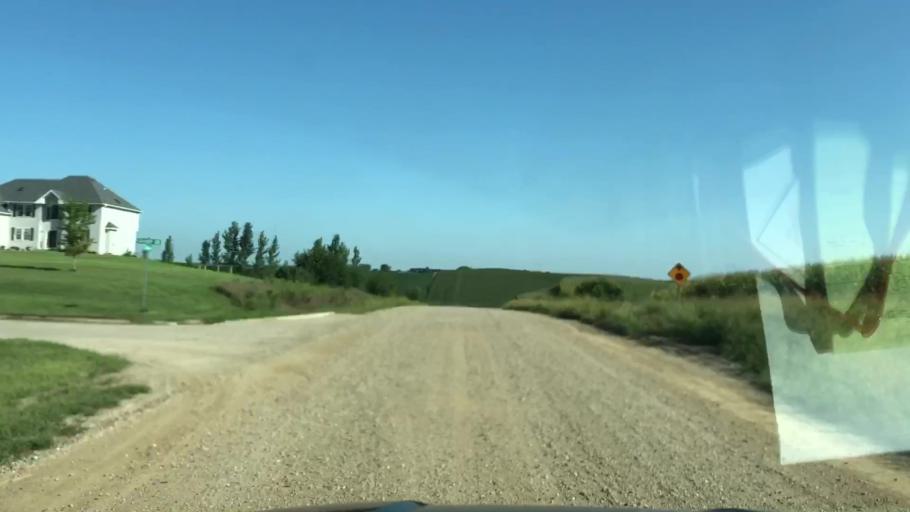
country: US
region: Iowa
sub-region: Woodbury County
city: Sergeant Bluff
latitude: 42.4720
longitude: -96.2921
